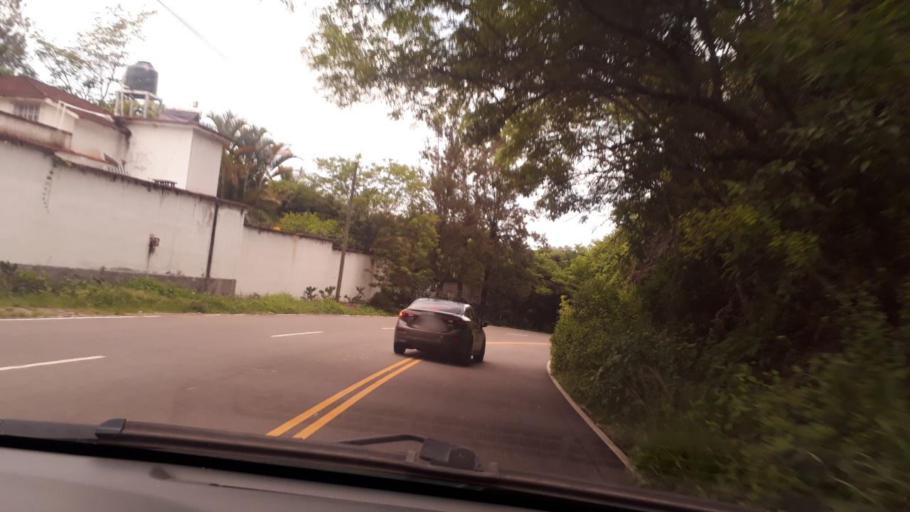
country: GT
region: Chiquimula
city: Esquipulas
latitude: 14.5603
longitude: -89.3655
